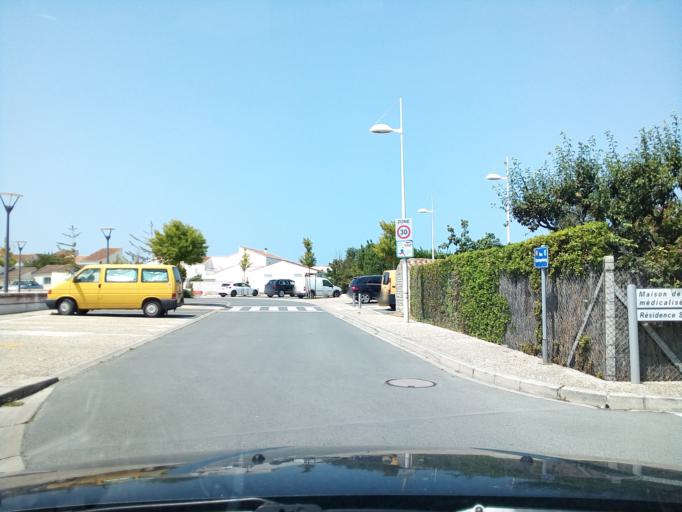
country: FR
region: Poitou-Charentes
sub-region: Departement de la Charente-Maritime
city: Dolus-d'Oleron
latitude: 45.9462
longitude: -1.3060
